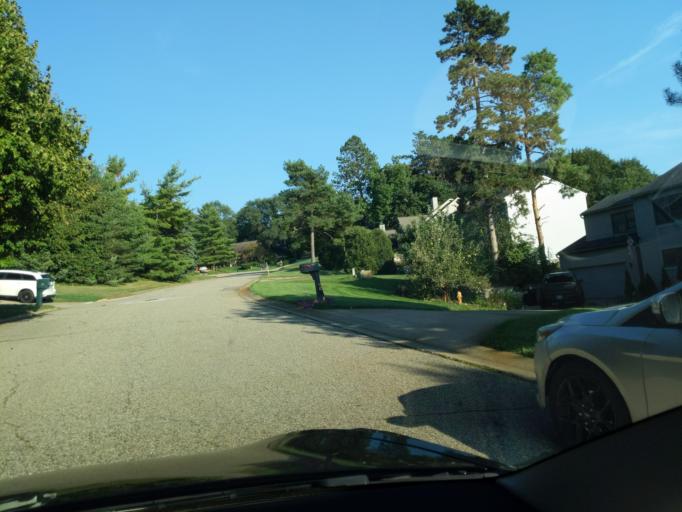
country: US
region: Michigan
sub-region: Livingston County
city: Whitmore Lake
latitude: 42.4447
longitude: -83.7493
